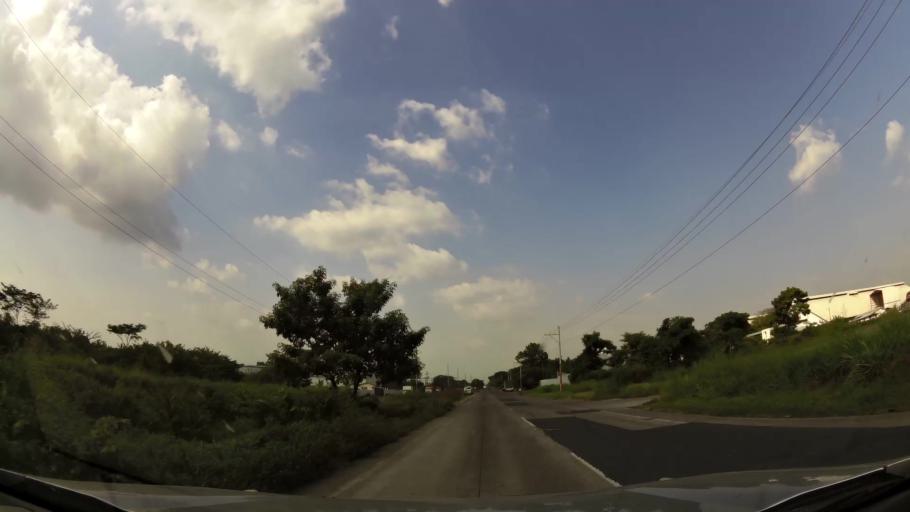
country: GT
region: Escuintla
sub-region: Municipio de Masagua
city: Masagua
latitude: 14.0989
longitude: -90.7798
